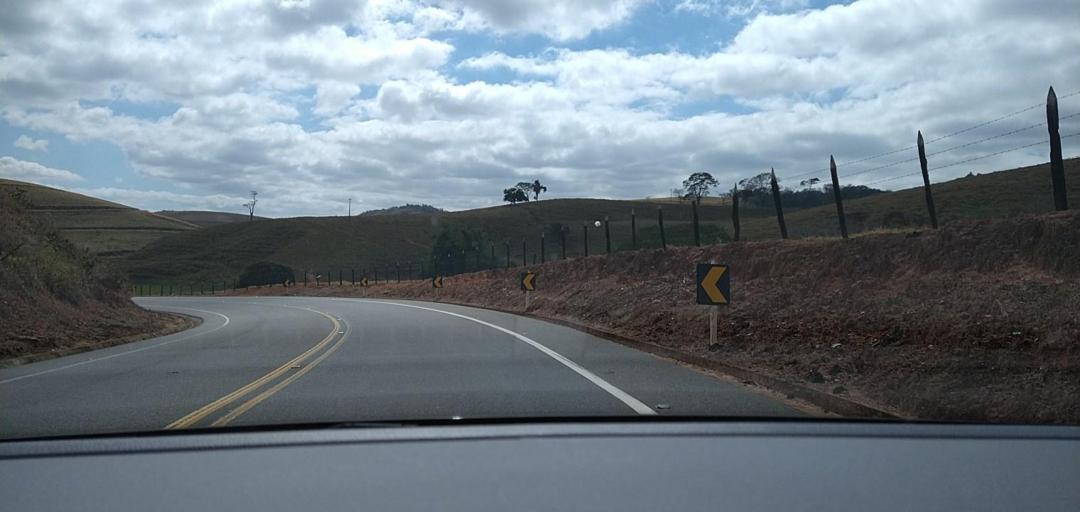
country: BR
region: Minas Gerais
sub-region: Ponte Nova
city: Ponte Nova
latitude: -20.4867
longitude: -42.8786
